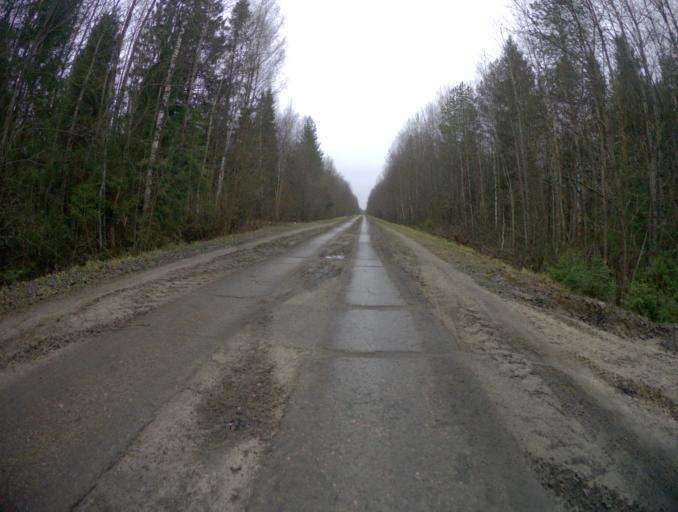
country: RU
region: Vladimir
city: Kommunar
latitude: 56.0337
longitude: 40.5130
